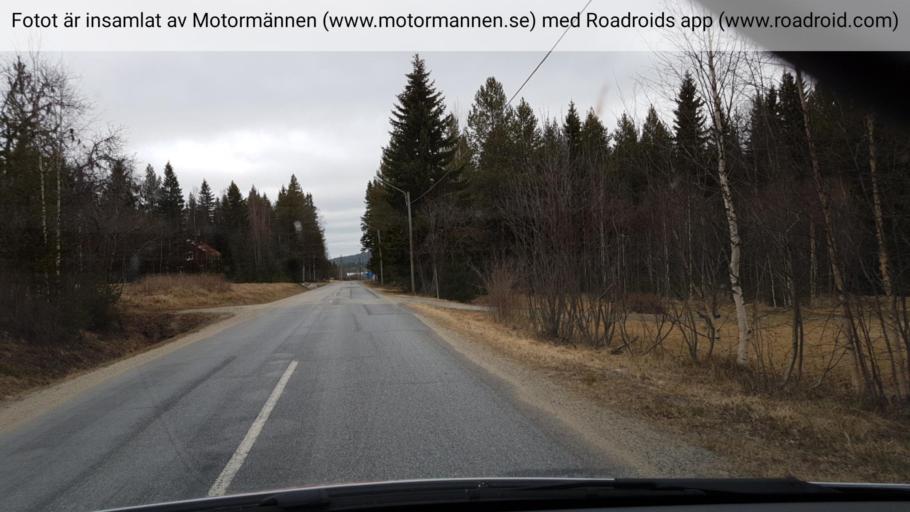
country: SE
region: Vaesterbotten
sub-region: Lycksele Kommun
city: Lycksele
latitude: 64.0640
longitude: 18.4000
